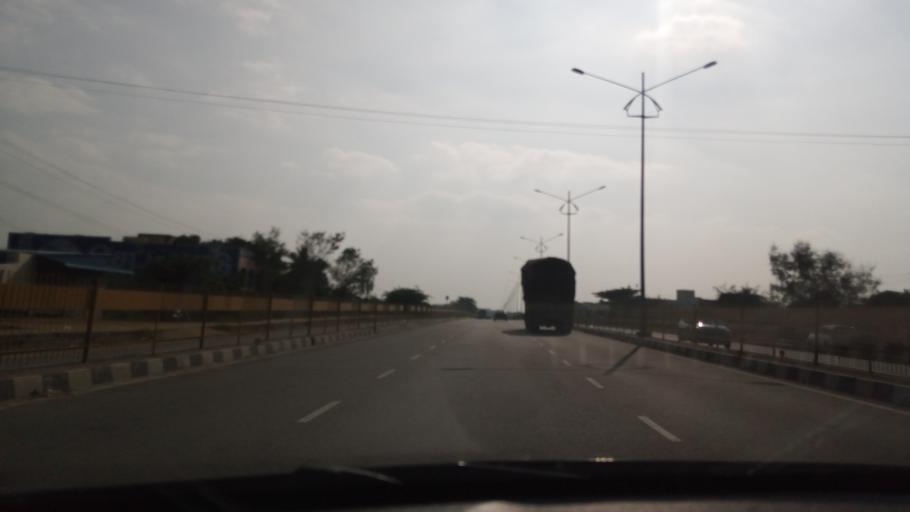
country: IN
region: Tamil Nadu
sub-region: Vellore
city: Vaniyambadi
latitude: 12.6702
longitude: 78.6164
